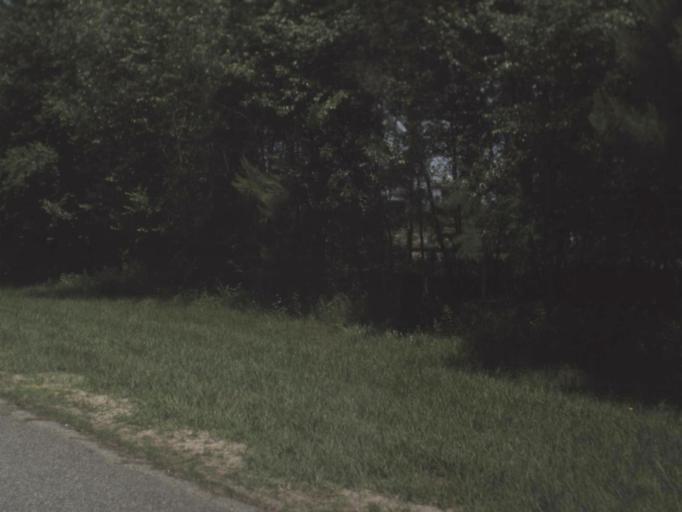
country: US
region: Florida
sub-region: Suwannee County
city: Live Oak
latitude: 30.3524
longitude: -83.1100
